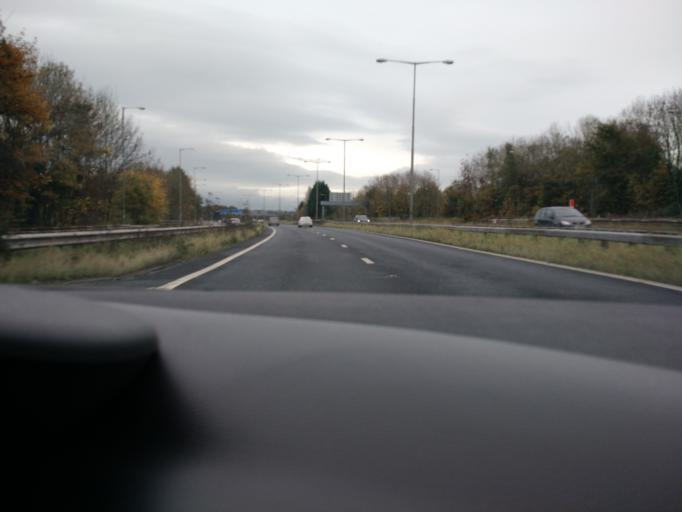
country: GB
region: England
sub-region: Lancashire
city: Preston
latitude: 53.8022
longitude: -2.7118
